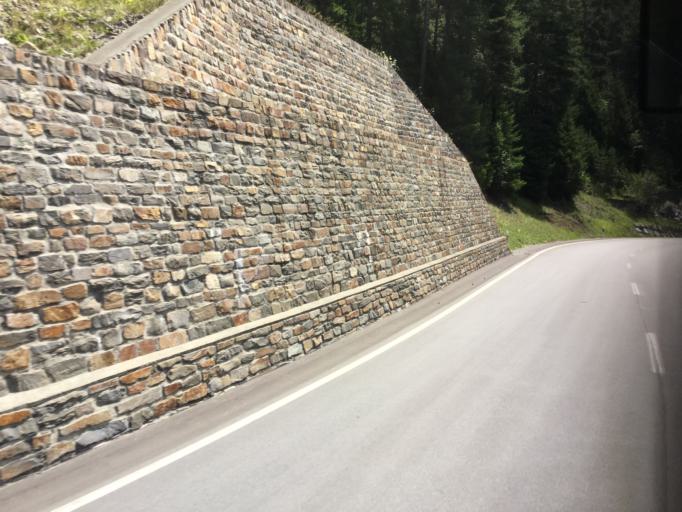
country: CH
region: Grisons
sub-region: Albula District
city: Tiefencastel
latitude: 46.6418
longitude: 9.5857
